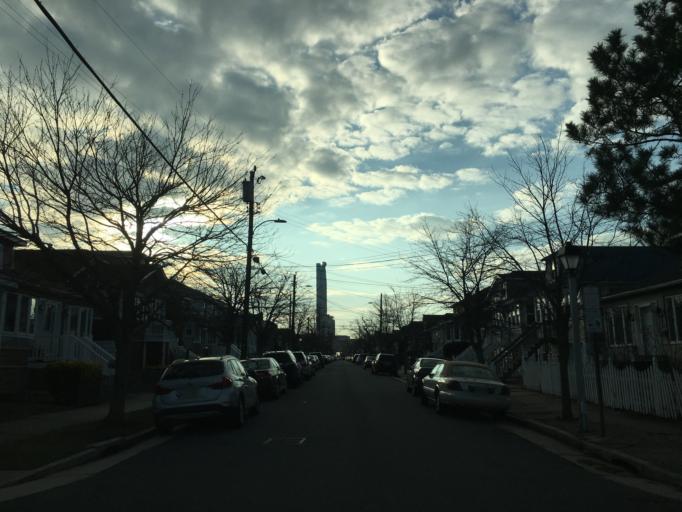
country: US
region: New Jersey
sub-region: Atlantic County
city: Atlantic City
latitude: 39.3736
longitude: -74.4230
